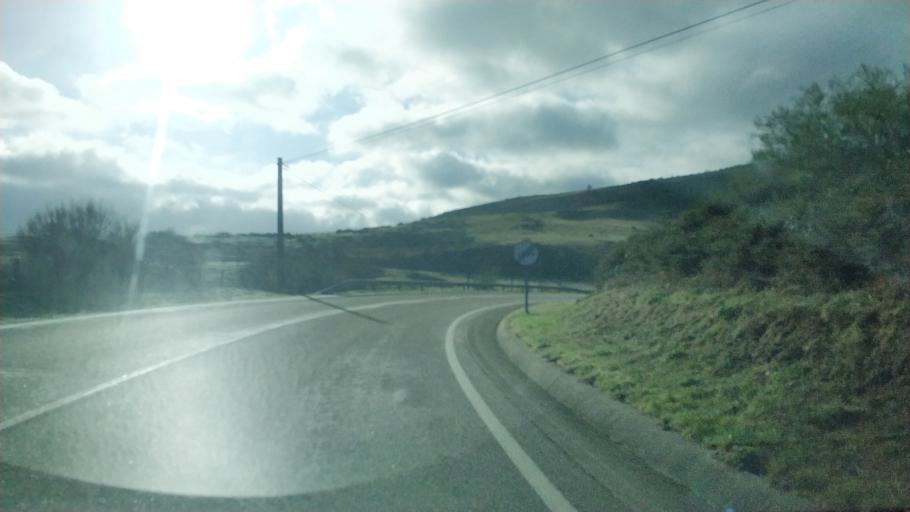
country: ES
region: Cantabria
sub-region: Provincia de Cantabria
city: Reinosa
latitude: 42.9721
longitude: -4.0788
